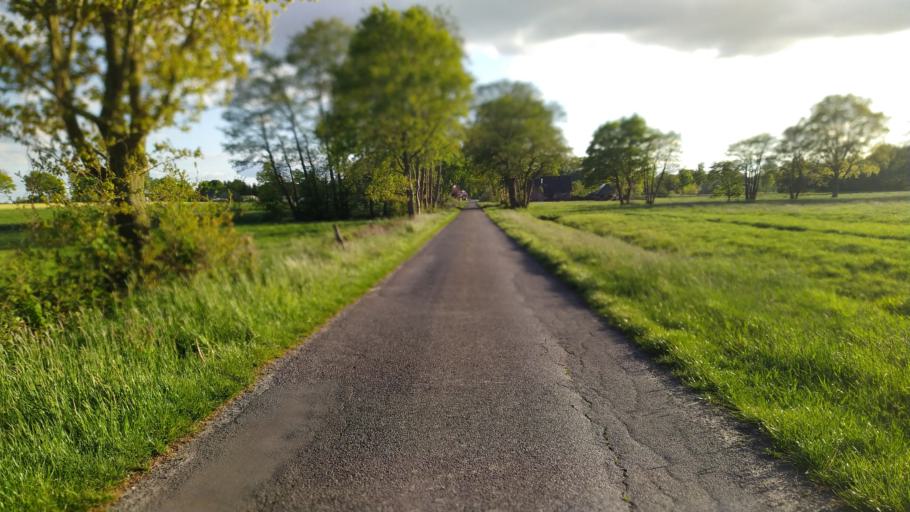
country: DE
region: Lower Saxony
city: Farven
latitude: 53.4403
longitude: 9.3307
